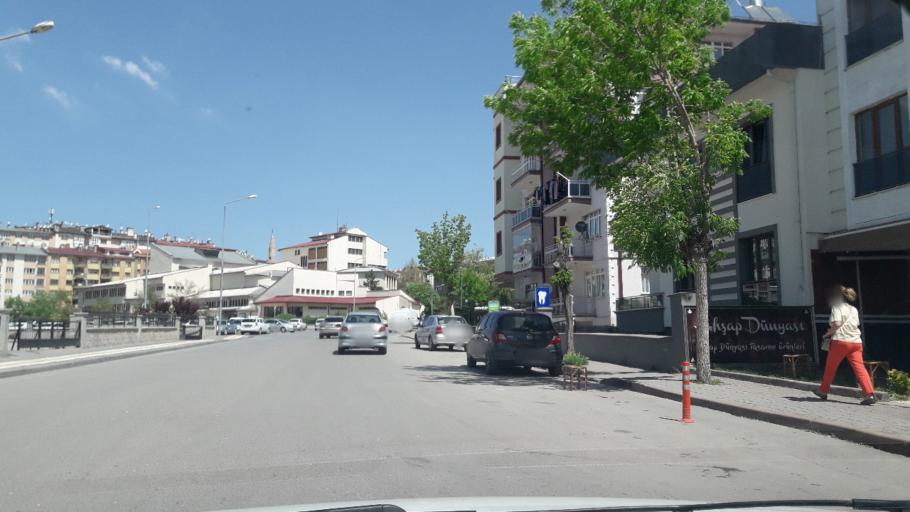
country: TR
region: Sivas
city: Sivas
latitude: 39.7421
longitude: 37.0122
